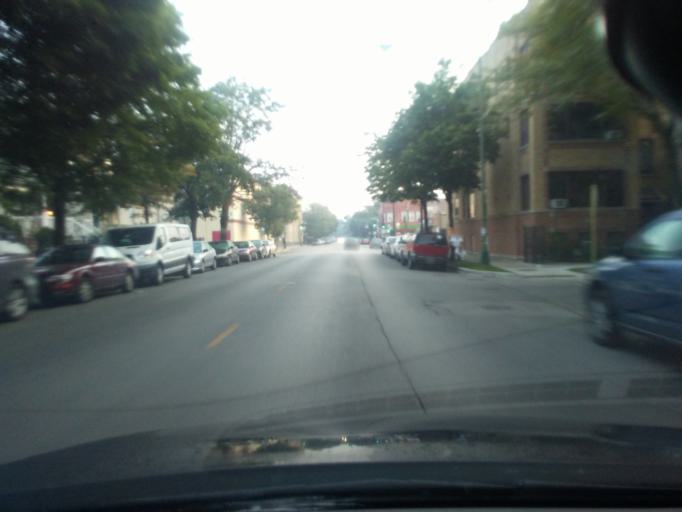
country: US
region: Illinois
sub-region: Cook County
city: Oak Park
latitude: 41.9236
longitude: -87.7169
